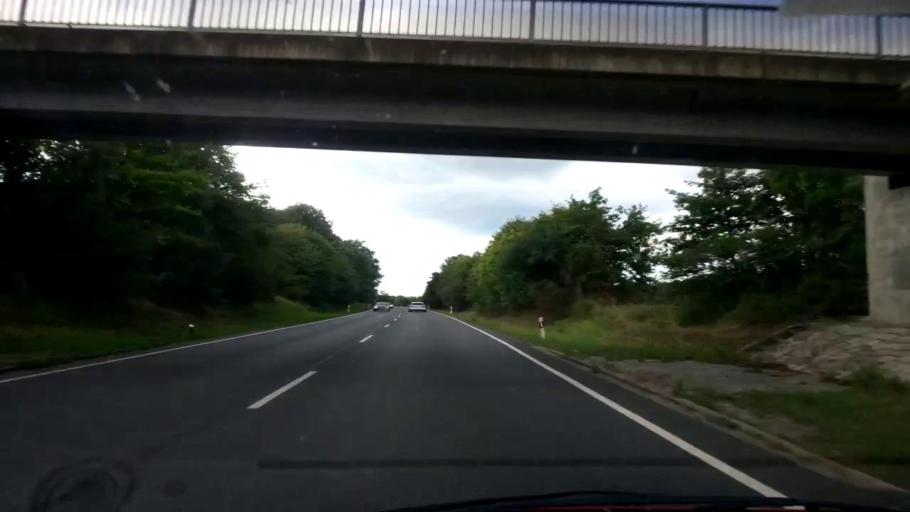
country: DE
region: Bavaria
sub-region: Regierungsbezirk Mittelfranken
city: Adelsdorf
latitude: 49.7003
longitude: 10.8968
